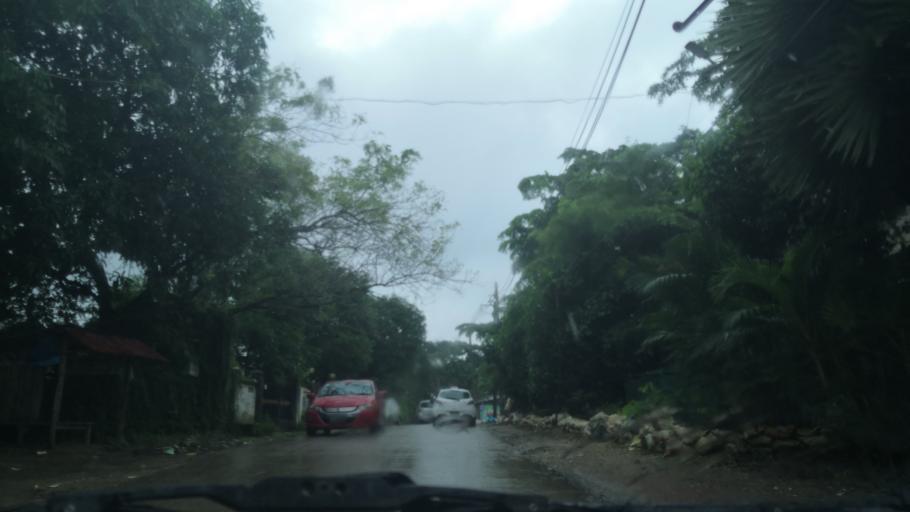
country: MM
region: Yangon
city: Yangon
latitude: 16.8863
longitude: 96.1498
